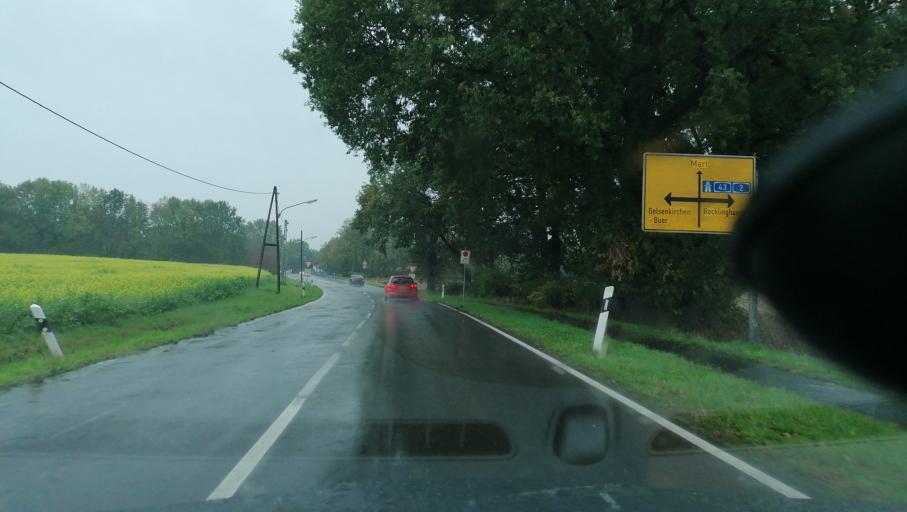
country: DE
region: North Rhine-Westphalia
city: Herten
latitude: 51.6158
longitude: 7.1636
